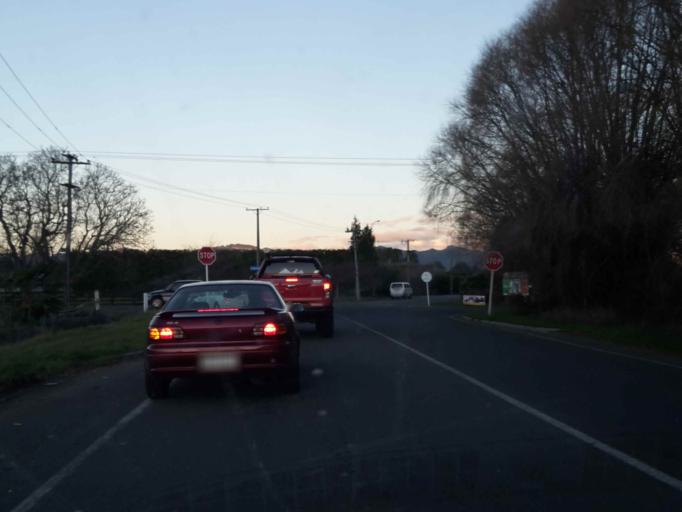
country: NZ
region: Canterbury
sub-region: Selwyn District
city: Prebbleton
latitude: -43.5693
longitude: 172.5206
